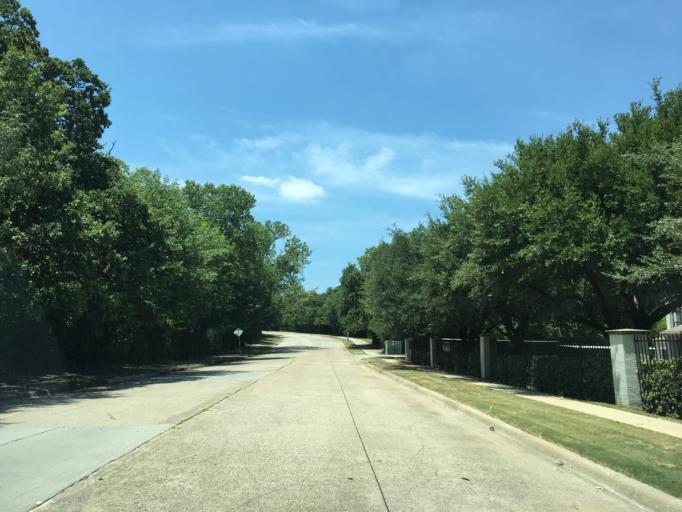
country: US
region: Texas
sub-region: Denton County
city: Lewisville
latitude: 33.0094
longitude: -96.9864
